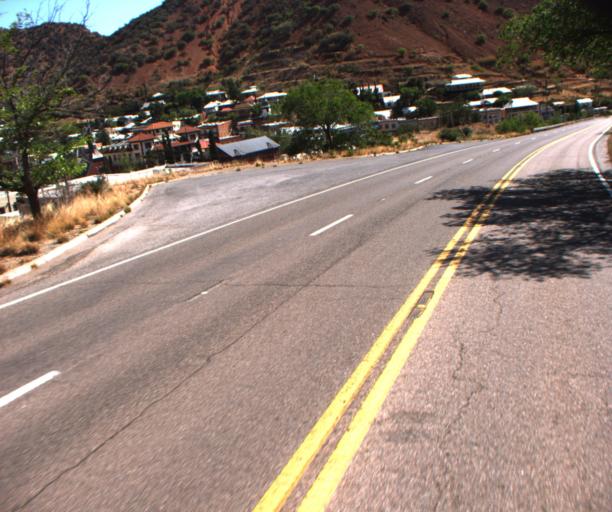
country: US
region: Arizona
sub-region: Cochise County
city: Bisbee
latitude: 31.4409
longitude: -109.9162
